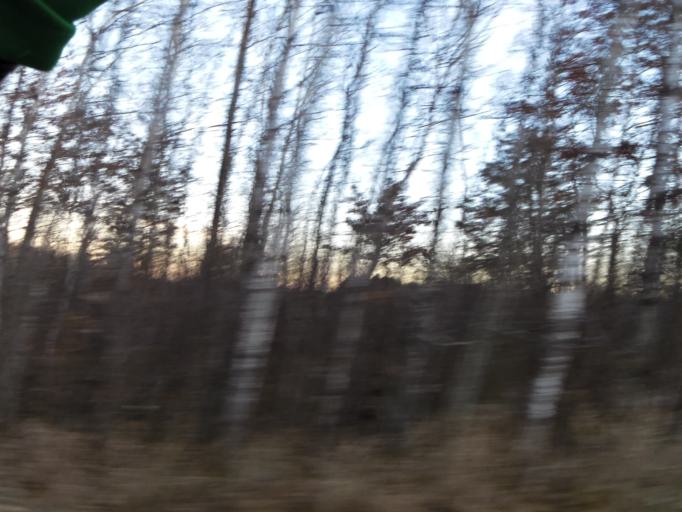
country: US
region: Minnesota
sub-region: Washington County
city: Grant
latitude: 45.0958
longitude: -92.8755
